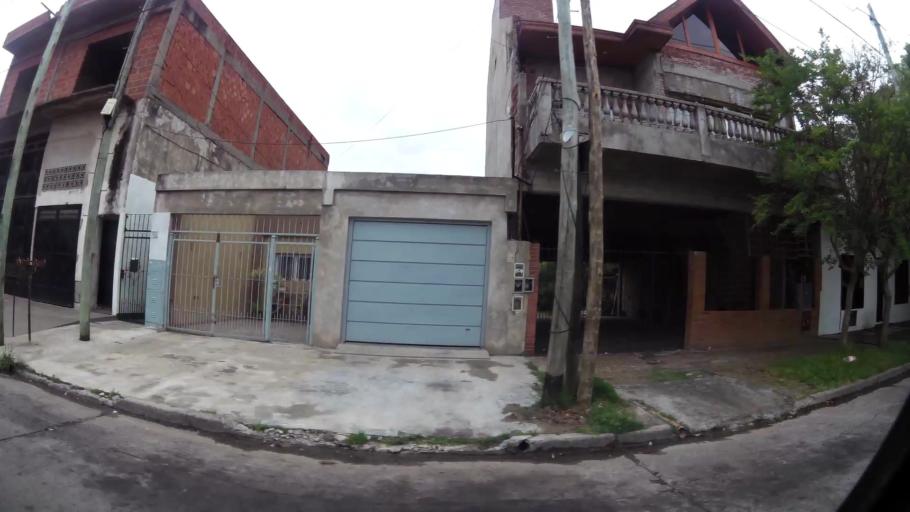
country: AR
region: Buenos Aires
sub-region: Partido de Lanus
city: Lanus
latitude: -34.7020
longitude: -58.3725
